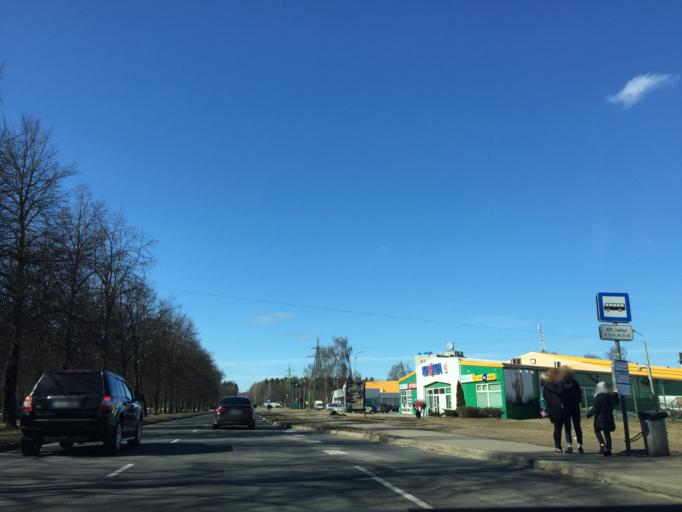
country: LV
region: Marupe
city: Marupe
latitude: 56.9632
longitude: 24.0305
